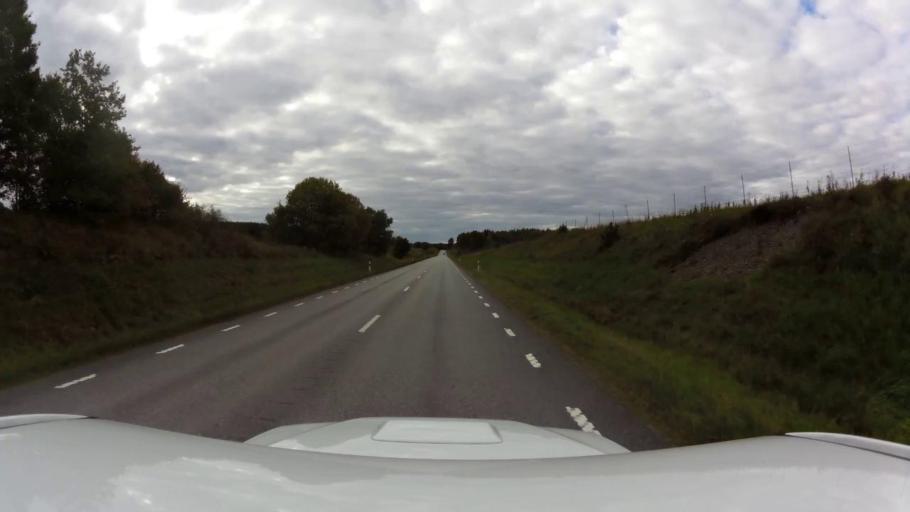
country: SE
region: OEstergoetland
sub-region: Kinda Kommun
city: Rimforsa
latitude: 58.2006
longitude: 15.6680
